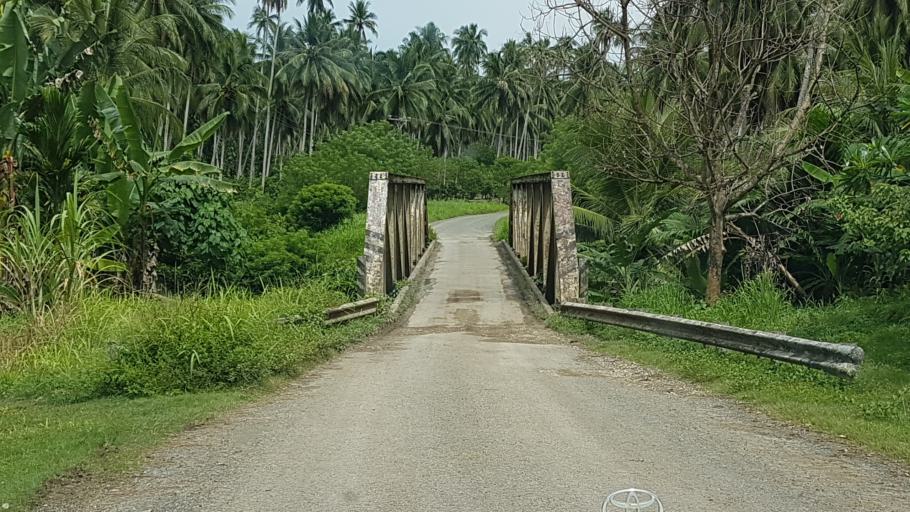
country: PG
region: Madang
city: Madang
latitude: -4.7918
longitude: 145.7162
